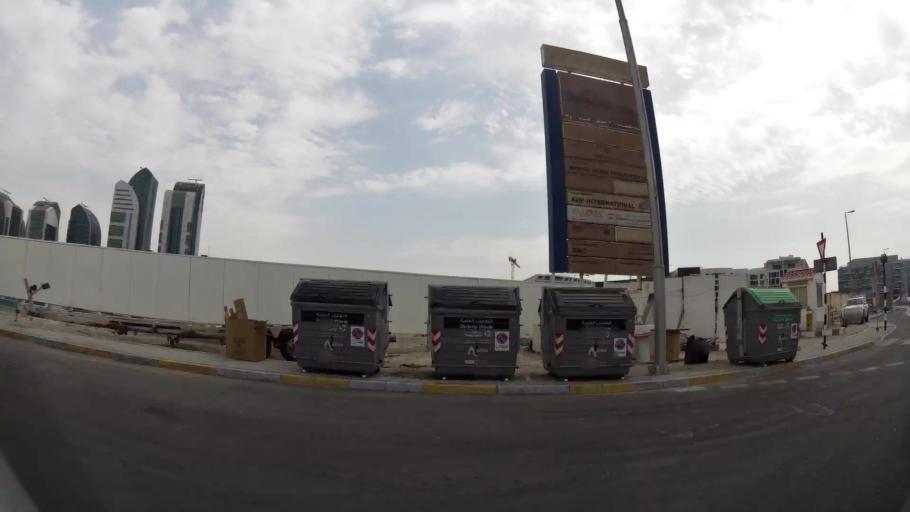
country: AE
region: Abu Dhabi
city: Abu Dhabi
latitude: 24.4546
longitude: 54.3346
